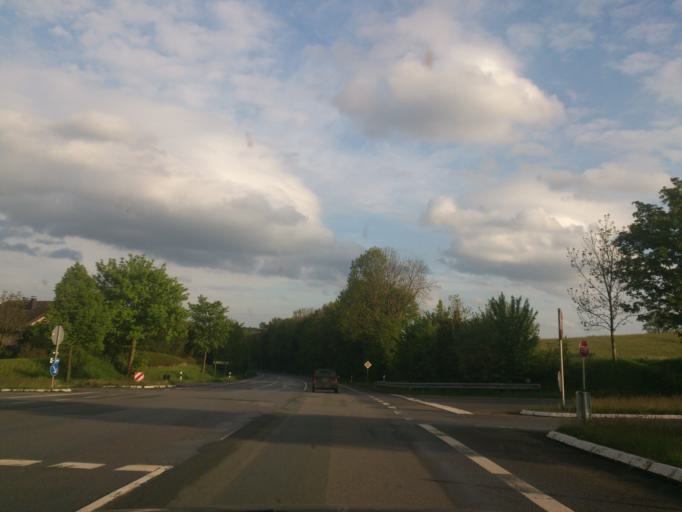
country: DE
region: North Rhine-Westphalia
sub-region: Regierungsbezirk Detmold
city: Bad Driburg
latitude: 51.6755
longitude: 8.9897
